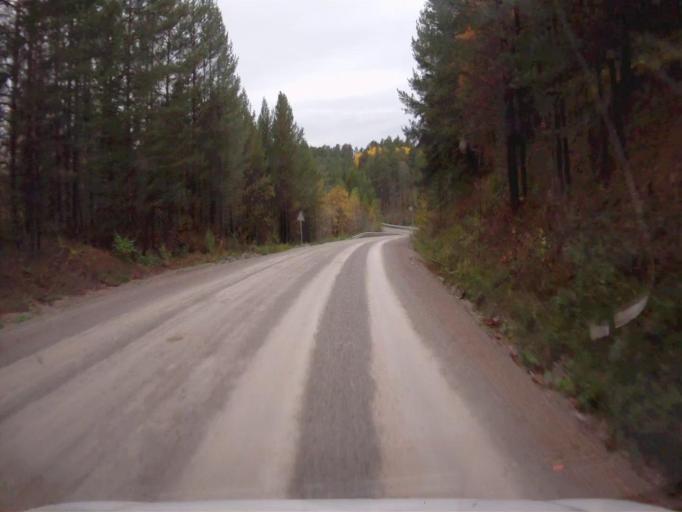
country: RU
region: Chelyabinsk
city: Nyazepetrovsk
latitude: 56.0590
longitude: 59.4535
